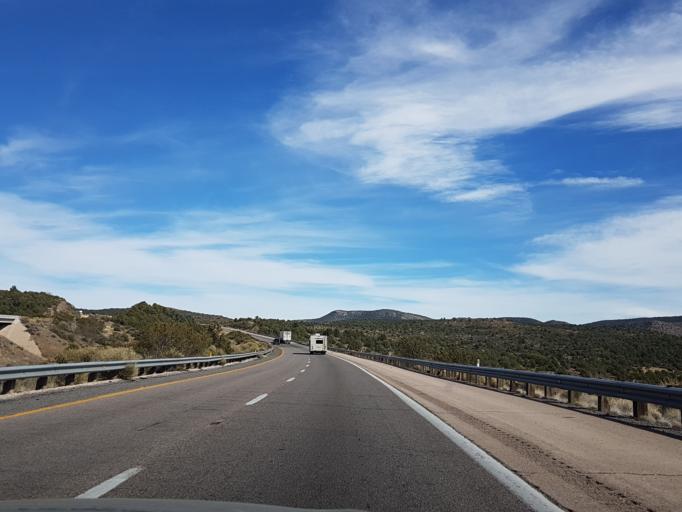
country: US
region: Arizona
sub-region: Mohave County
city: Peach Springs
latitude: 35.1890
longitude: -113.3191
